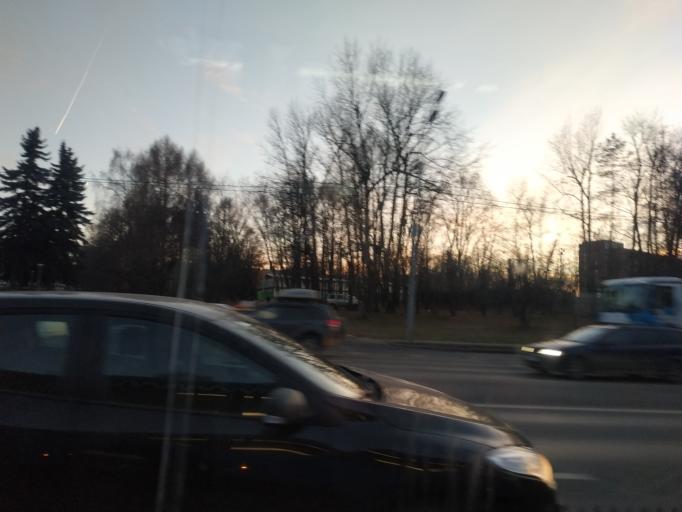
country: RU
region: Moscow
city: Zyuzino
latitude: 55.6506
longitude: 37.5568
